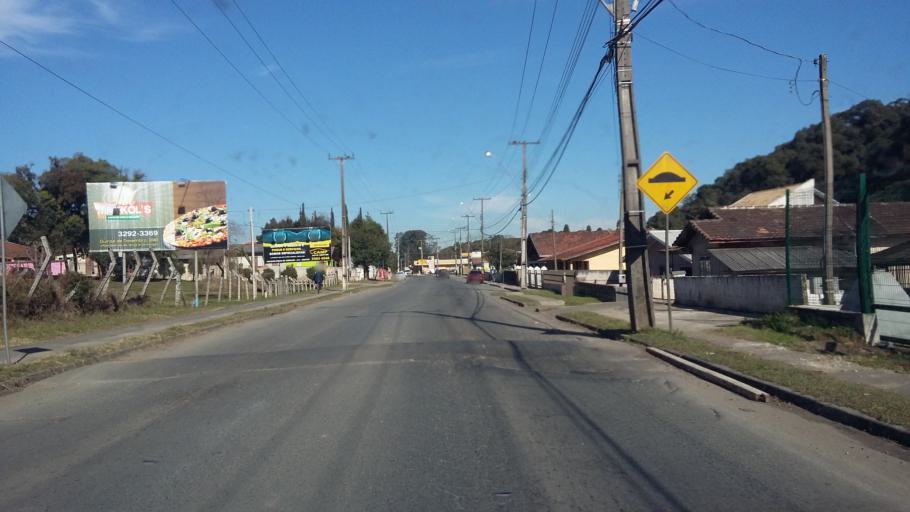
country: BR
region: Parana
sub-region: Campo Largo
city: Campo Largo
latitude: -25.4664
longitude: -49.5644
